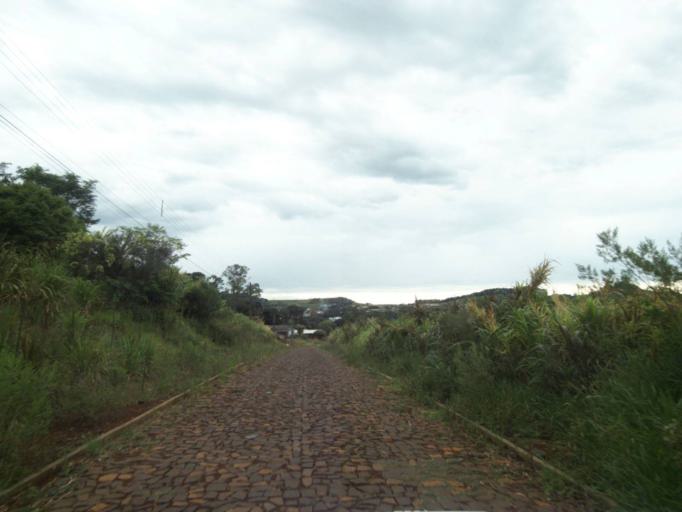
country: BR
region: Parana
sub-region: Guaraniacu
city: Guaraniacu
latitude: -25.1059
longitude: -52.8600
